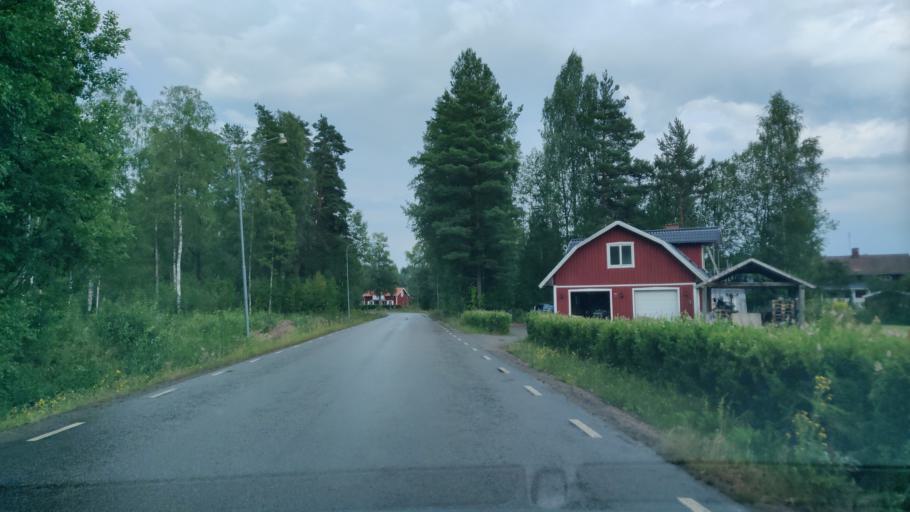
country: SE
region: Vaermland
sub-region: Munkfors Kommun
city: Munkfors
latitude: 59.8513
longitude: 13.5504
